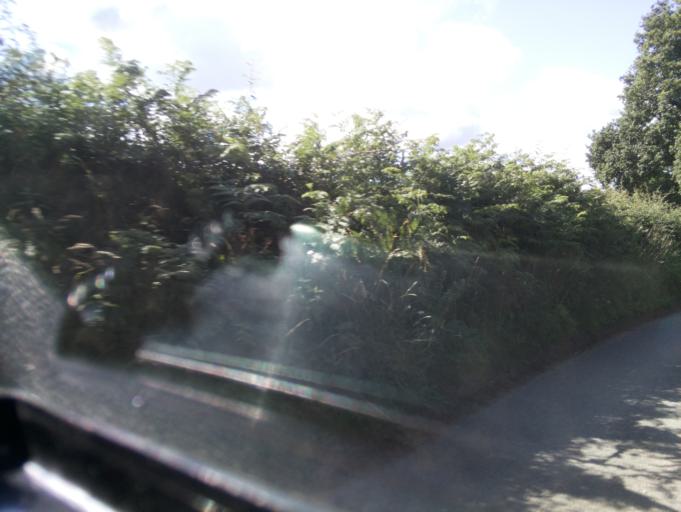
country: GB
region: England
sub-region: Gloucestershire
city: Newent
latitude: 51.9338
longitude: -2.4221
